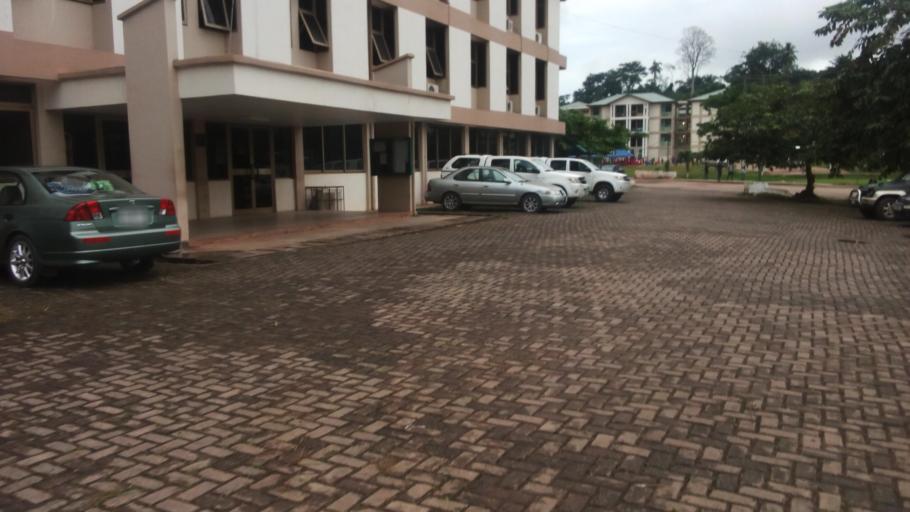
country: GH
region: Western
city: Tarkwa
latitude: 5.2985
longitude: -2.0016
